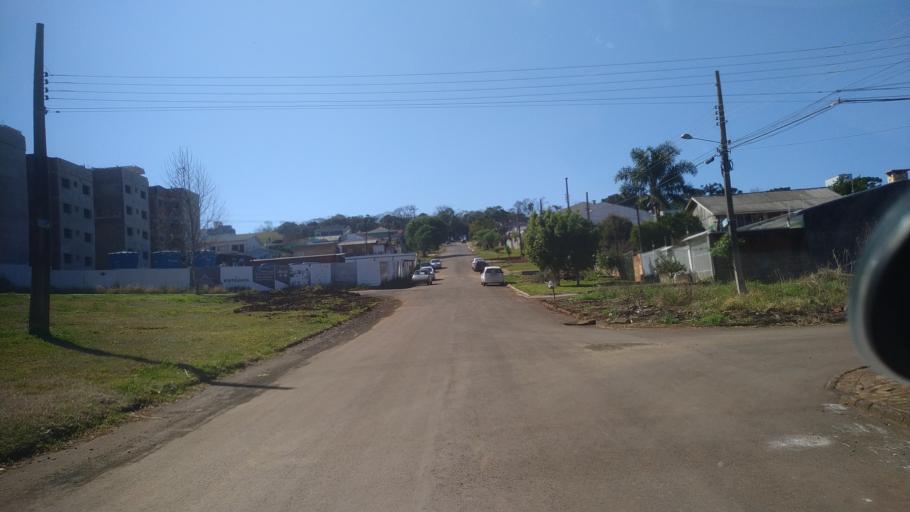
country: BR
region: Santa Catarina
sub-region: Chapeco
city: Chapeco
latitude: -27.0910
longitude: -52.5914
